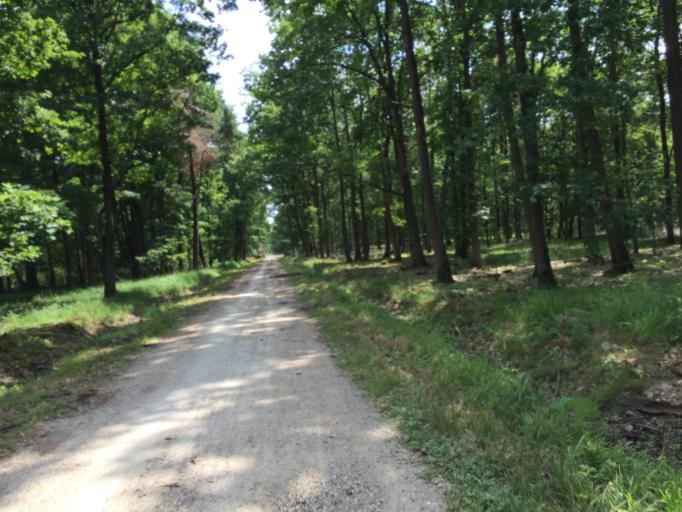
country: FR
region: Ile-de-France
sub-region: Departement de l'Essonne
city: Epinay-sous-Senart
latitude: 48.6678
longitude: 2.5005
